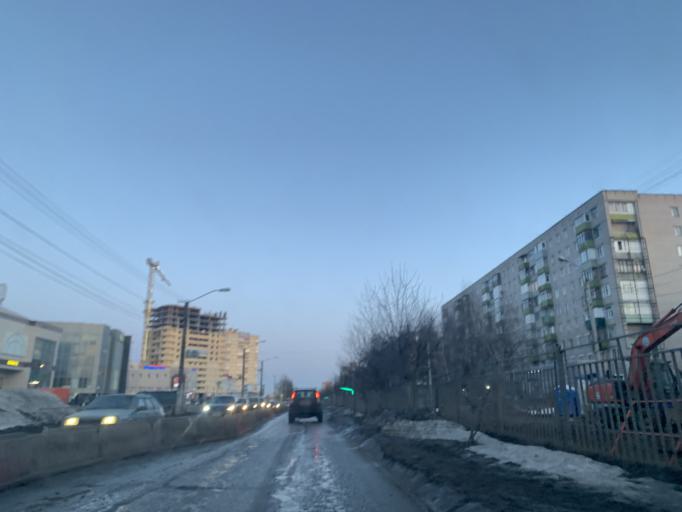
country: RU
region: Jaroslavl
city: Yaroslavl
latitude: 57.6495
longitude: 39.9499
